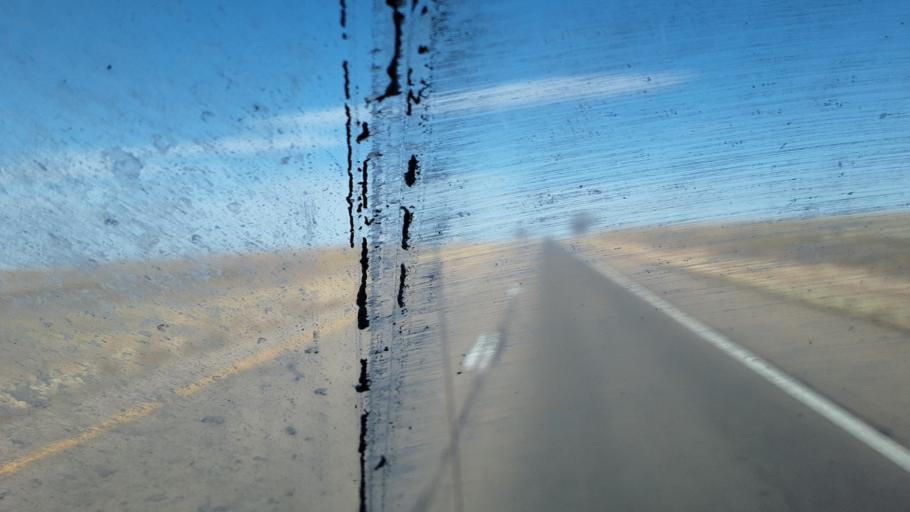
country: US
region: Colorado
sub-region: Weld County
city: Keenesburg
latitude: 40.1318
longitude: -104.4882
